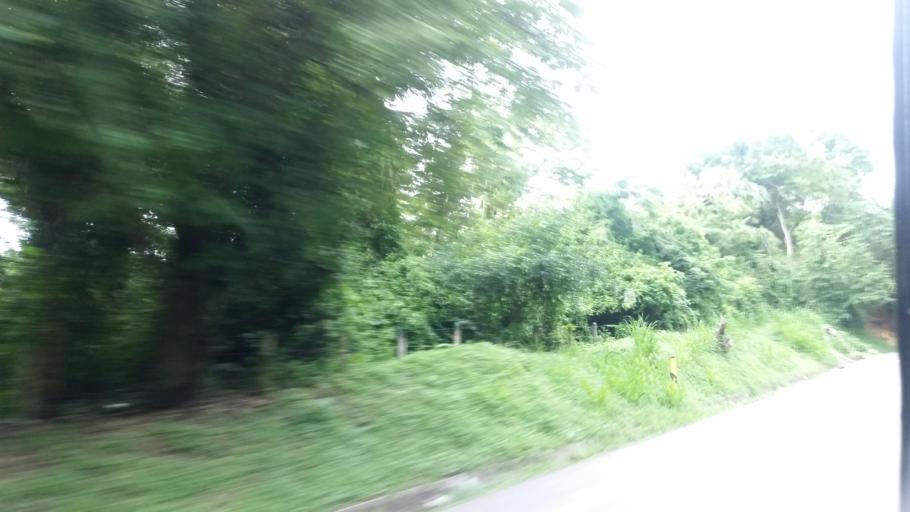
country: CO
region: Magdalena
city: Santa Marta
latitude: 11.2851
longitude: -73.8814
